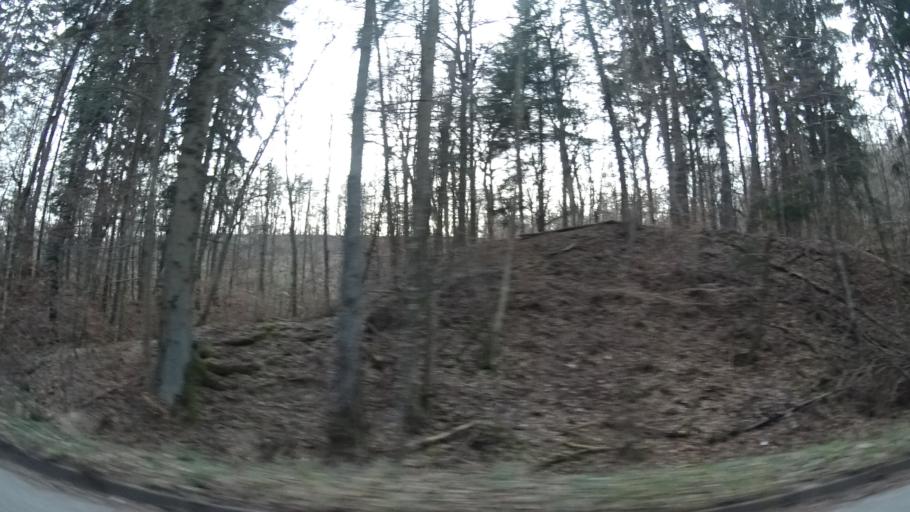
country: DE
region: Baden-Wuerttemberg
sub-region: Regierungsbezirk Stuttgart
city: Gerlingen
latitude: 48.7688
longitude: 9.0538
